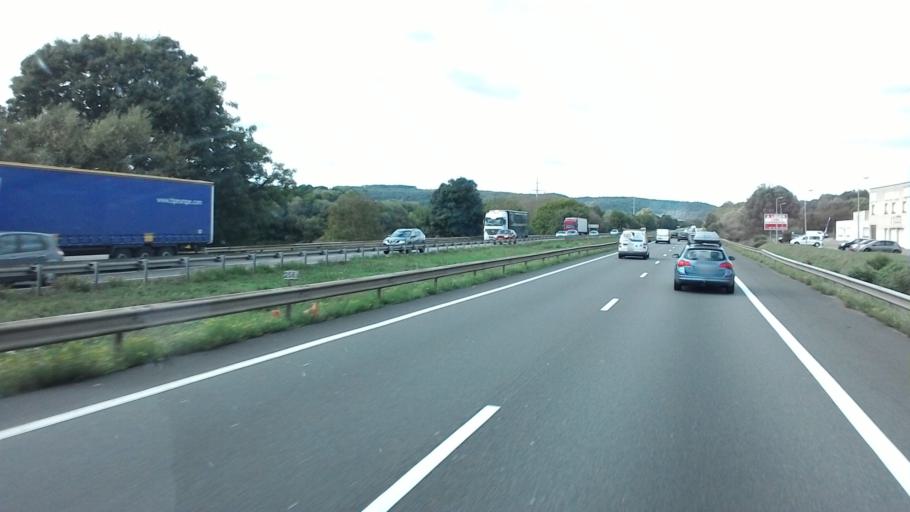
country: FR
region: Lorraine
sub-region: Departement de Meurthe-et-Moselle
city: Bouxieres-aux-Dames
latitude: 48.7577
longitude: 6.1523
